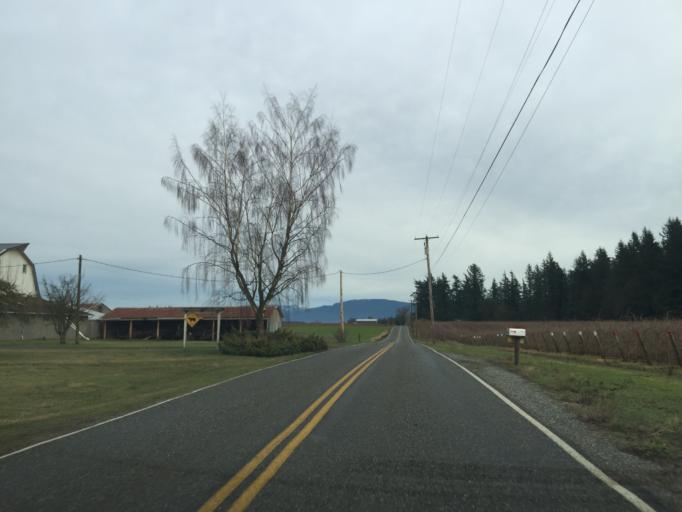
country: US
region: Washington
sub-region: Whatcom County
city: Ferndale
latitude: 48.8988
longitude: -122.5292
